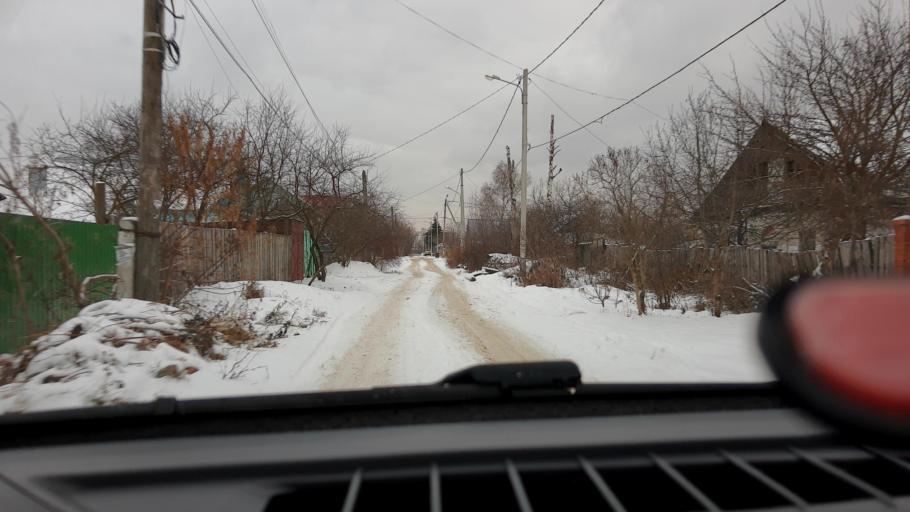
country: RU
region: Nizjnij Novgorod
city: Gorbatovka
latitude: 56.2694
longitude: 43.7664
